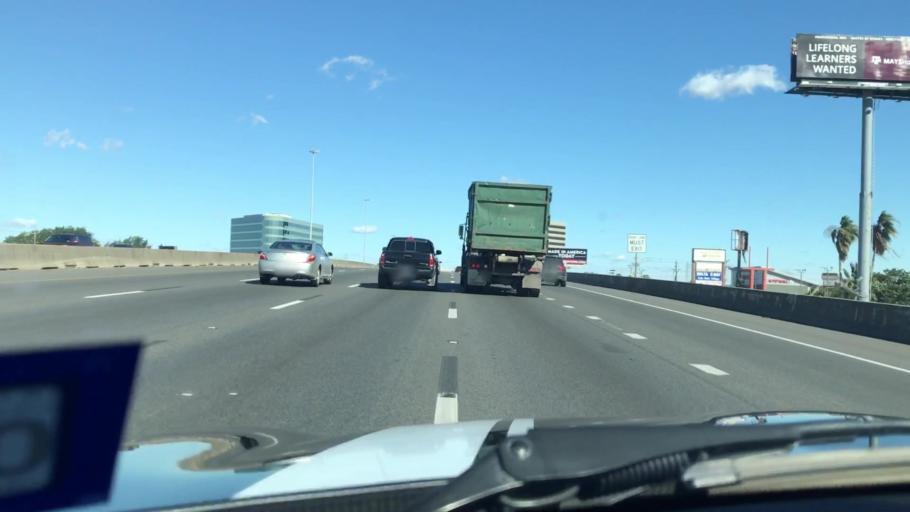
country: US
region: Texas
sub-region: Fort Bend County
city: Meadows Place
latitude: 29.6748
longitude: -95.5430
